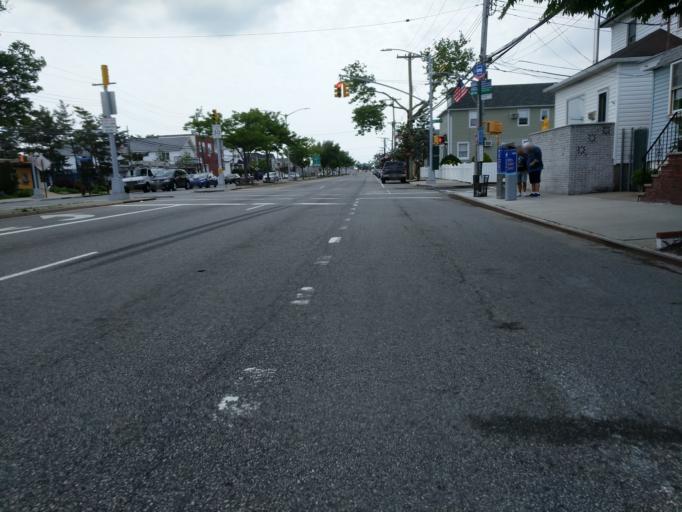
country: US
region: New York
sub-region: Nassau County
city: Inwood
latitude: 40.6012
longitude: -73.8205
